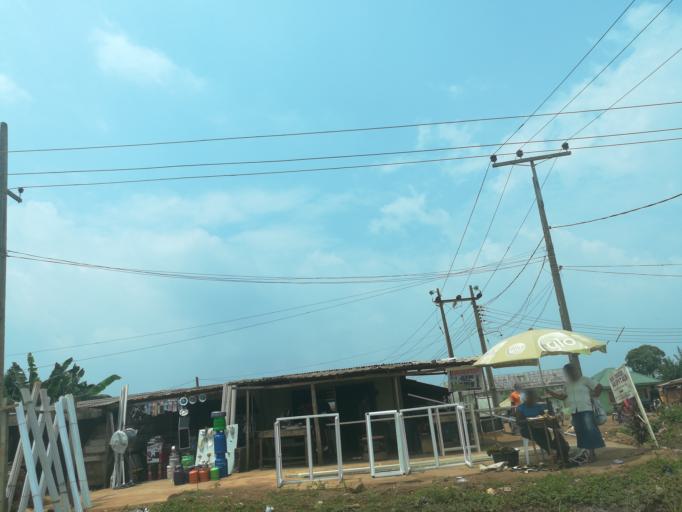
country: NG
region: Lagos
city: Ikorodu
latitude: 6.6037
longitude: 3.6058
